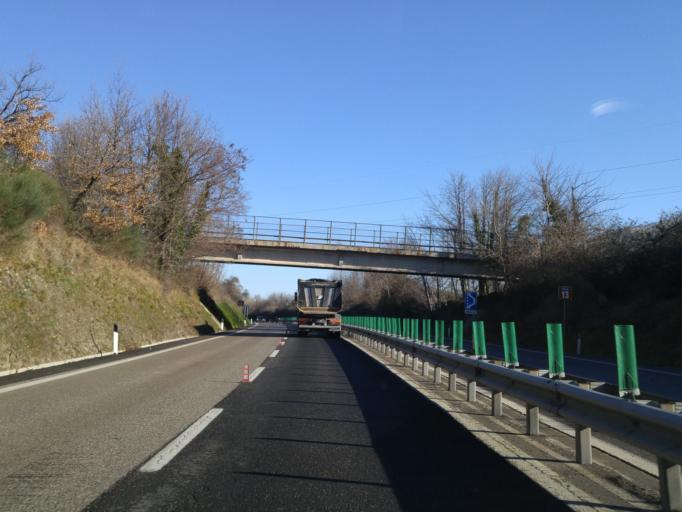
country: IT
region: The Marches
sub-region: Provincia di Pesaro e Urbino
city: Sant'Ippolito
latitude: 43.6909
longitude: 12.8573
